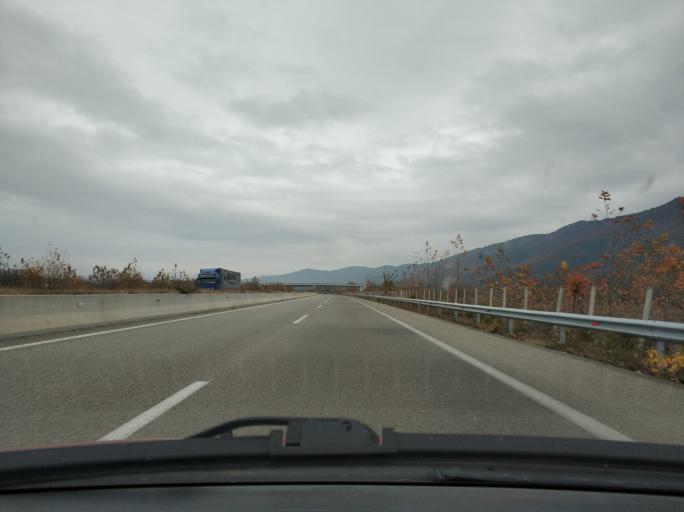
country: GR
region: East Macedonia and Thrace
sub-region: Nomos Kavalas
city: Eleftheres
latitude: 40.8654
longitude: 24.1877
